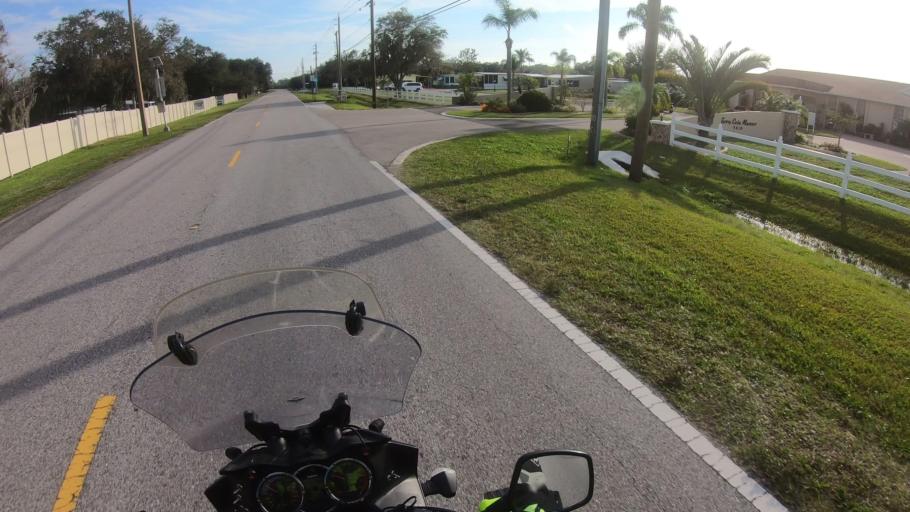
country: US
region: Florida
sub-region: Manatee County
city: Memphis
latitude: 27.5657
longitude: -82.5565
